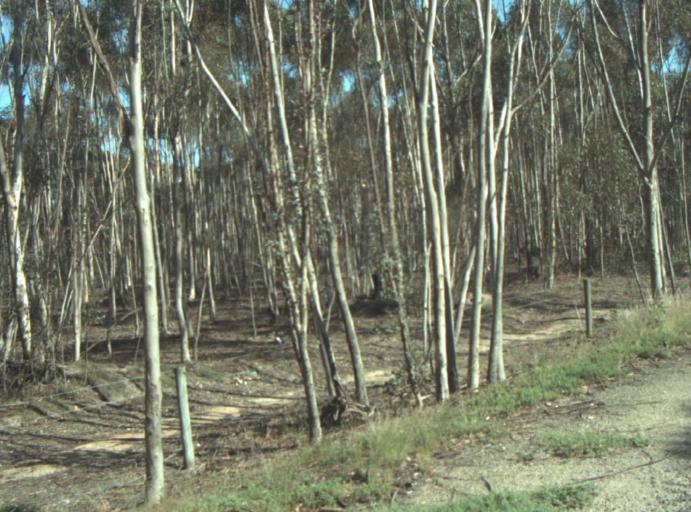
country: AU
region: Victoria
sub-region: Greater Geelong
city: Lara
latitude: -37.9459
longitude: 144.3917
